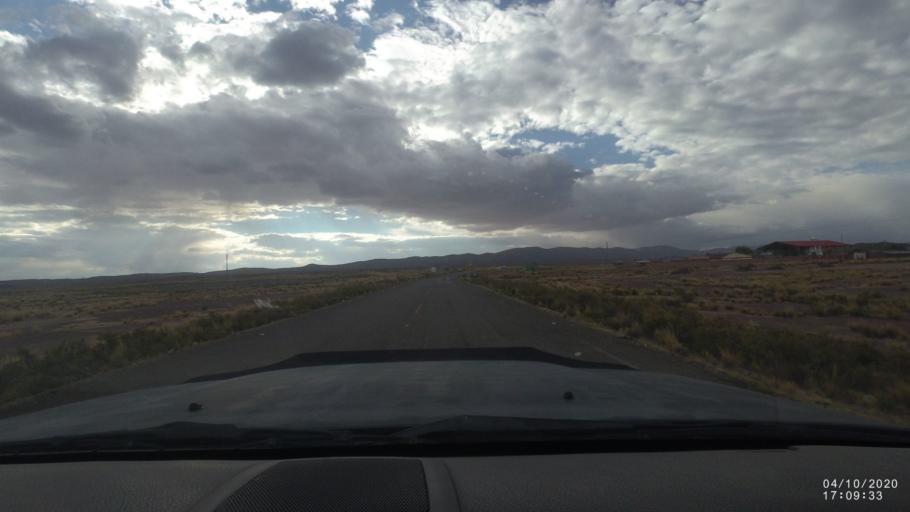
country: BO
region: Oruro
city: Oruro
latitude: -18.3381
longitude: -67.5853
